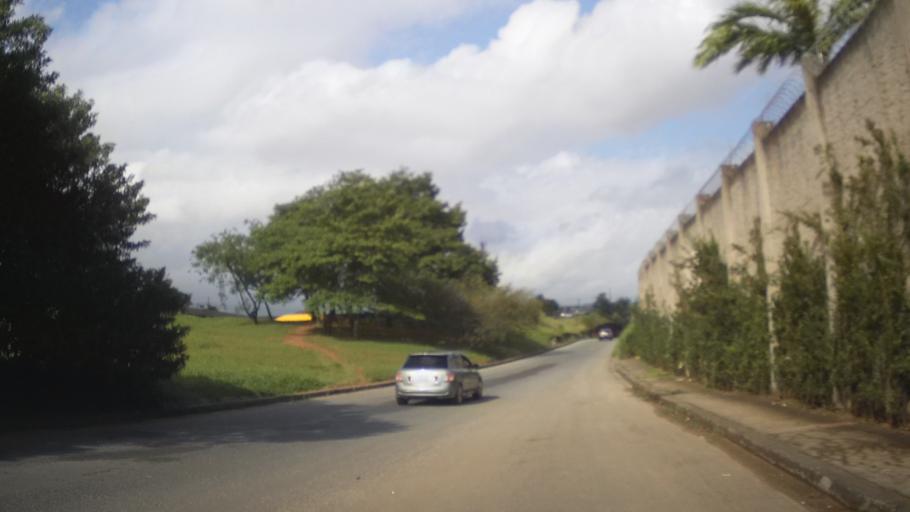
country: BR
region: Sao Paulo
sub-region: Guarulhos
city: Guarulhos
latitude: -23.4568
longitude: -46.4764
